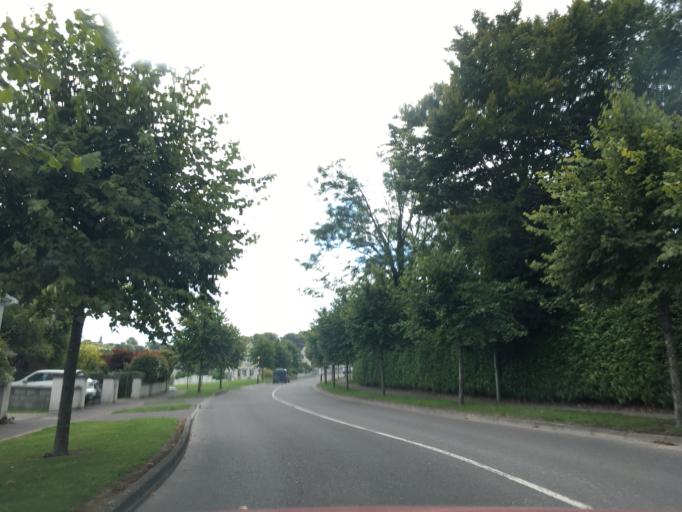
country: IE
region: Munster
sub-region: County Cork
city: Crosshaven
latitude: 51.7992
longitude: -8.2951
